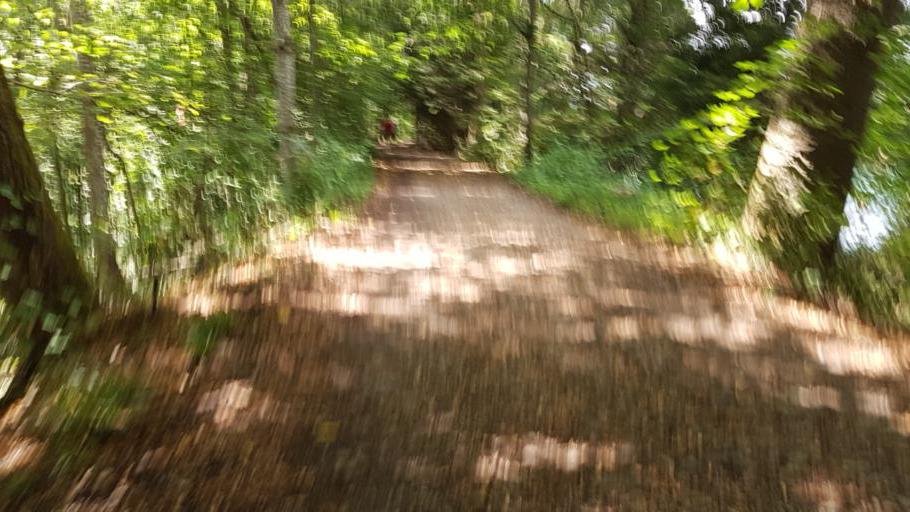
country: CH
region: Bern
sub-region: Bern-Mittelland District
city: Belp
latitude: 46.9111
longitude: 7.5081
